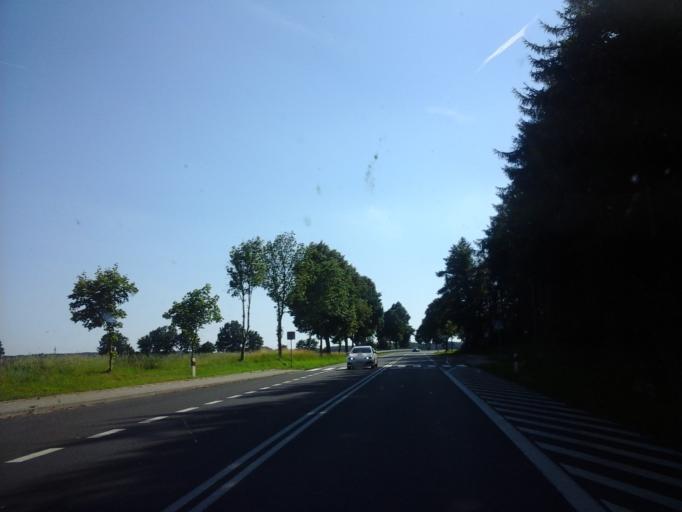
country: PL
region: West Pomeranian Voivodeship
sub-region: Powiat kolobrzeski
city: Ryman
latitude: 53.9587
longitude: 15.5687
